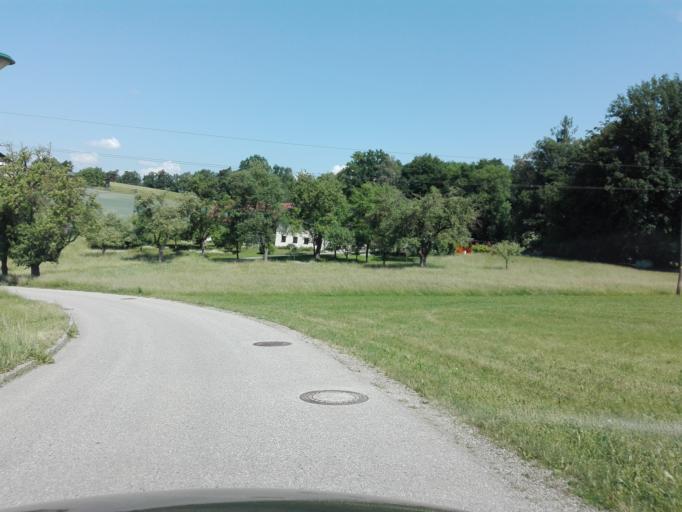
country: AT
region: Upper Austria
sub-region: Politischer Bezirk Linz-Land
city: Enns
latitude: 48.2818
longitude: 14.4769
